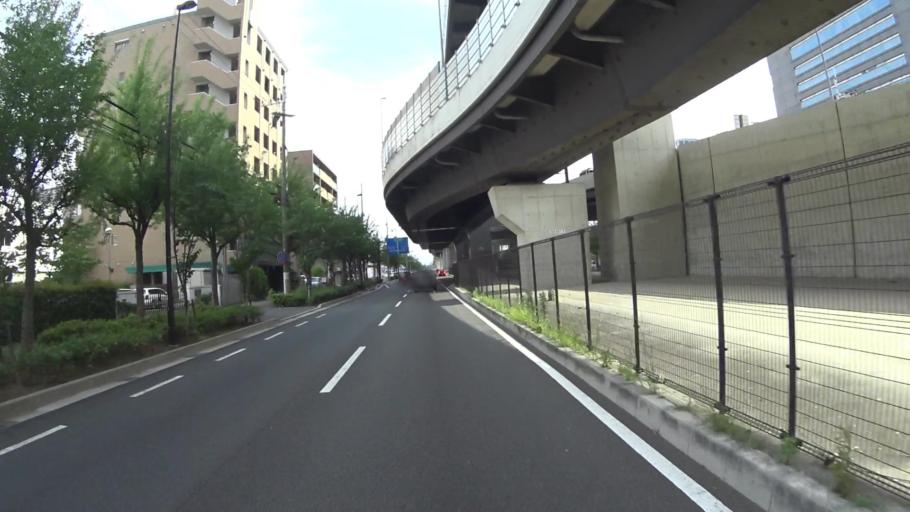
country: JP
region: Kyoto
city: Muko
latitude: 34.9478
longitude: 135.7520
